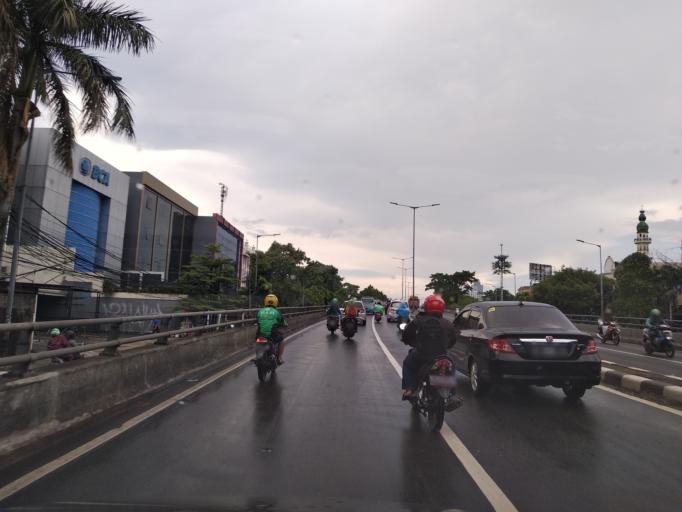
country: ID
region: Jakarta Raya
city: Jakarta
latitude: -6.2253
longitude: 106.8609
